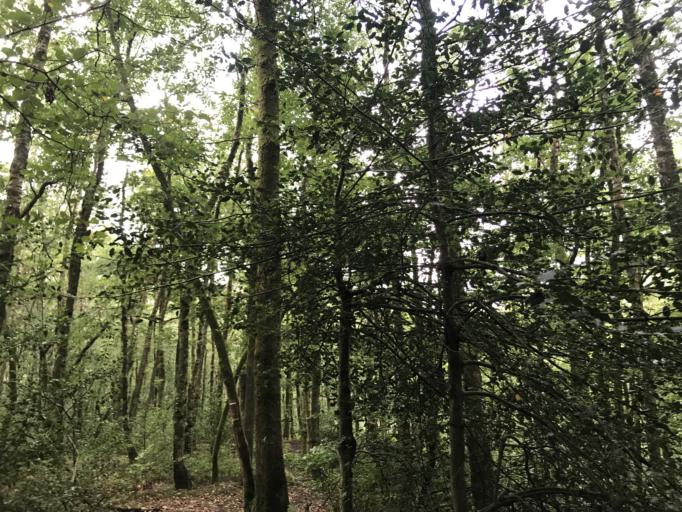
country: FR
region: Champagne-Ardenne
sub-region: Departement des Ardennes
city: Thilay
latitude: 49.8811
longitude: 4.7836
